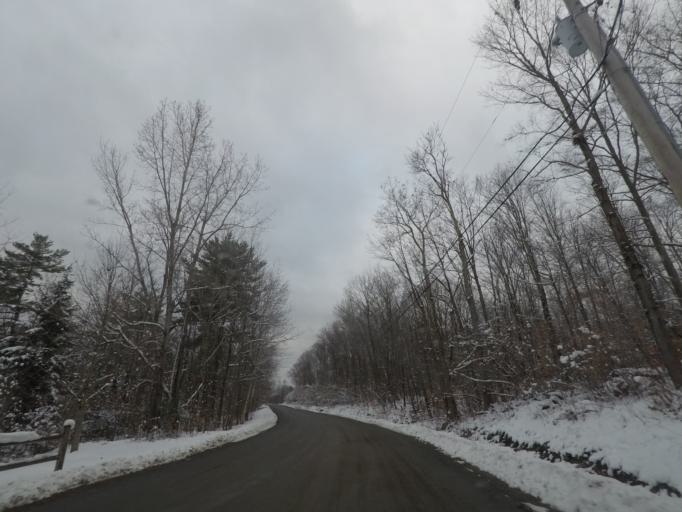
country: US
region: New York
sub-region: Rensselaer County
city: Averill Park
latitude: 42.6600
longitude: -73.5321
